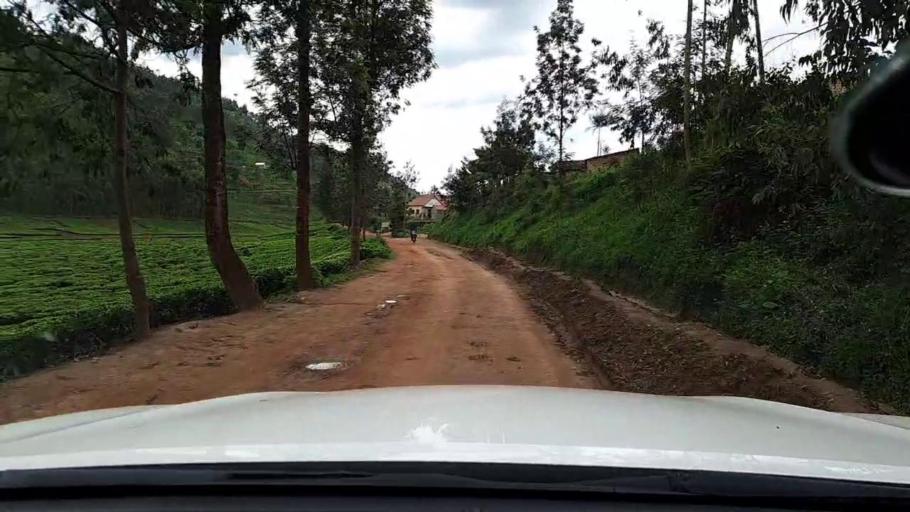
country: RW
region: Northern Province
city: Byumba
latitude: -1.6572
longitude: 29.9098
